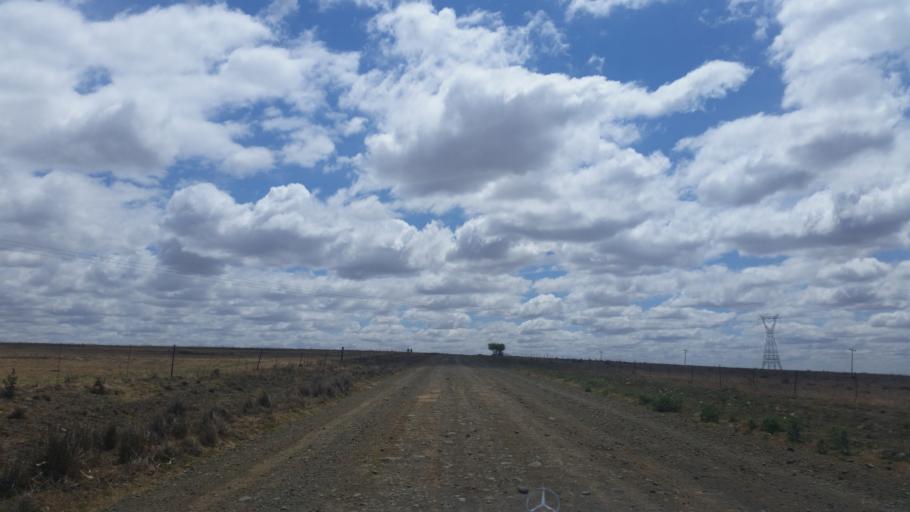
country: ZA
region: Orange Free State
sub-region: Thabo Mofutsanyana District Municipality
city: Harrismith
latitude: -28.2437
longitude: 28.9292
